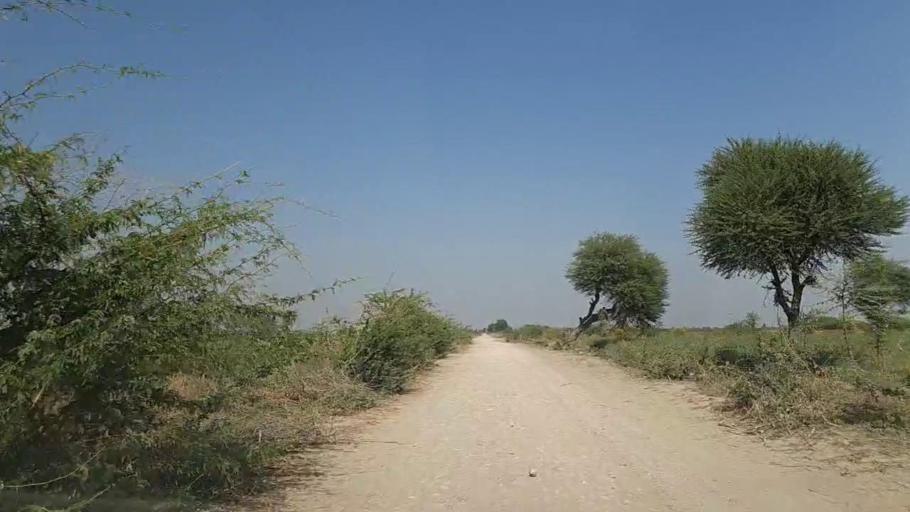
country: PK
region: Sindh
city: Samaro
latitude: 25.2038
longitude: 69.4042
